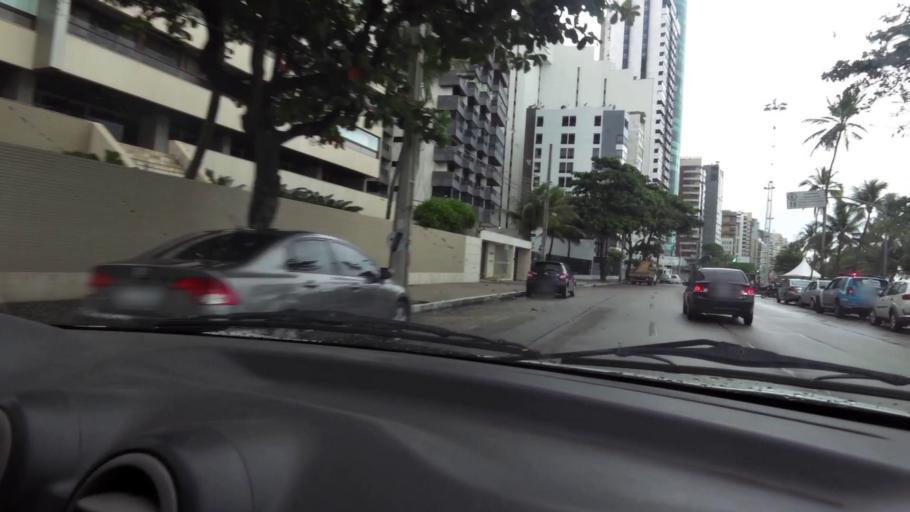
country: BR
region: Pernambuco
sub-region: Recife
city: Recife
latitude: -8.1233
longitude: -34.8966
